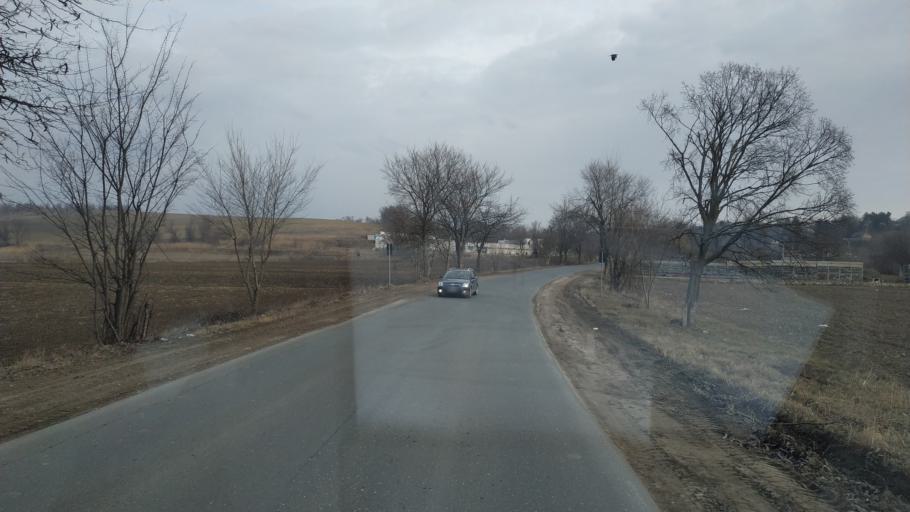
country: MD
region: Chisinau
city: Singera
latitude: 46.9246
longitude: 29.0474
